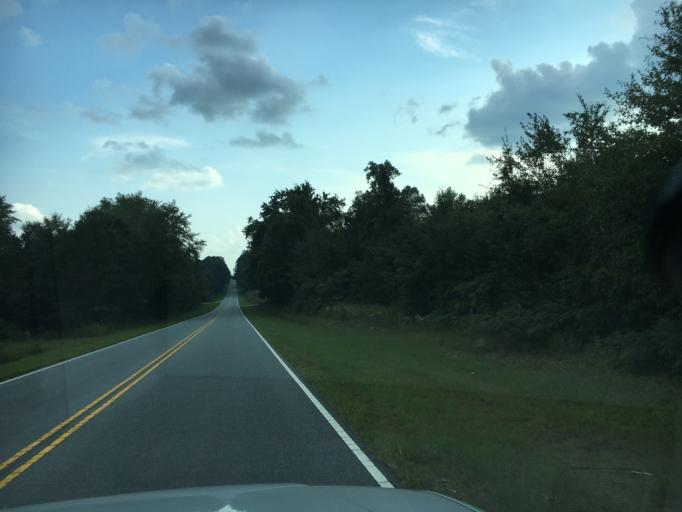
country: US
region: North Carolina
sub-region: Rutherford County
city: Rutherfordton
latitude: 35.4887
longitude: -81.9797
